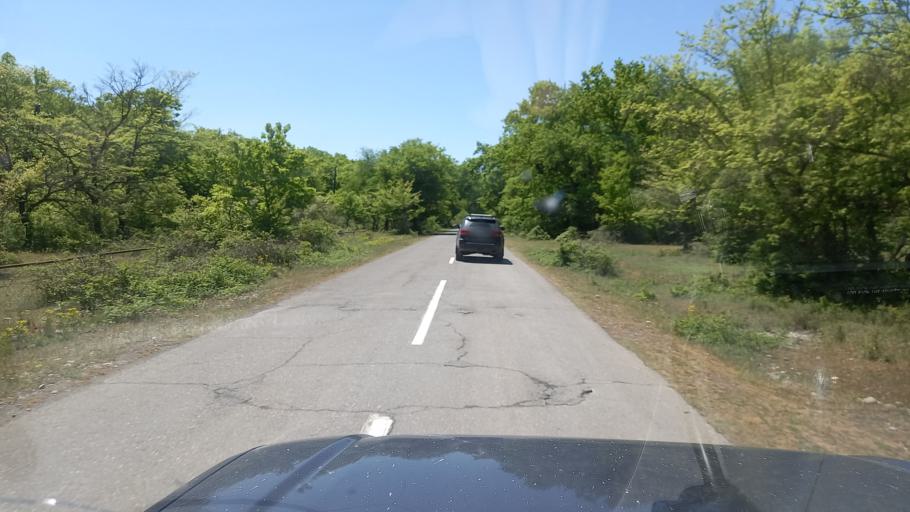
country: RU
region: Dagestan
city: Samur
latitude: 41.8425
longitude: 48.5744
